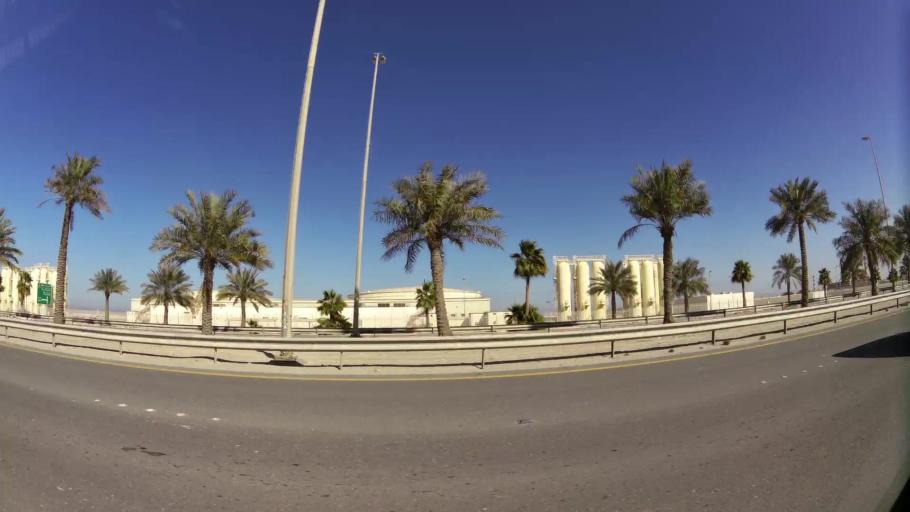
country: BH
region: Muharraq
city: Al Hadd
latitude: 26.2292
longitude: 50.6576
